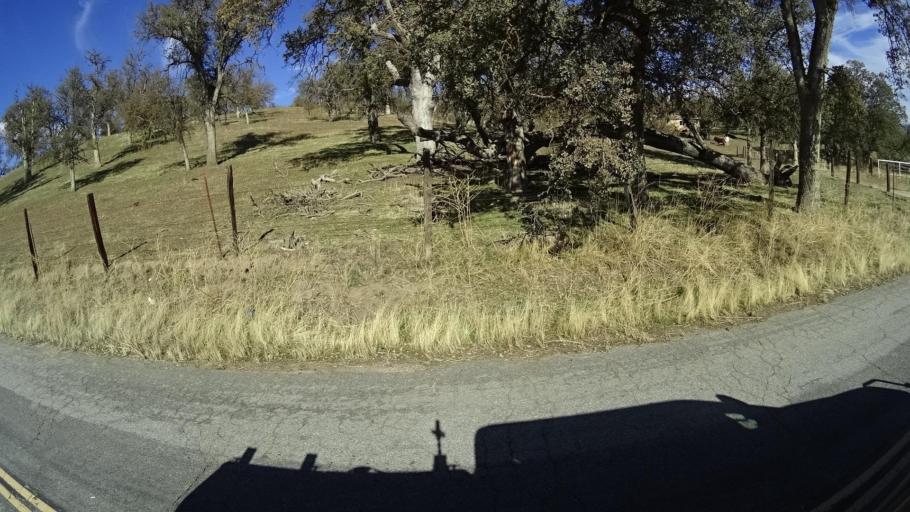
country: US
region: California
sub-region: Kern County
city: Alta Sierra
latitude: 35.6305
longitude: -118.7701
